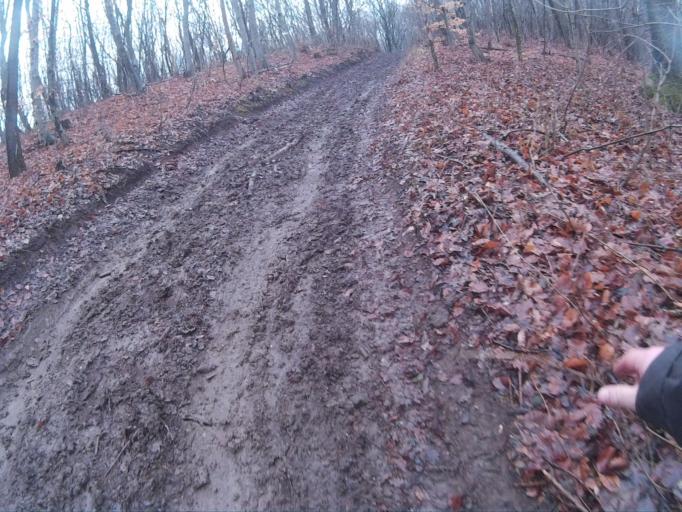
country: HU
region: Komarom-Esztergom
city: Bajna
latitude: 47.7051
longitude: 18.5721
